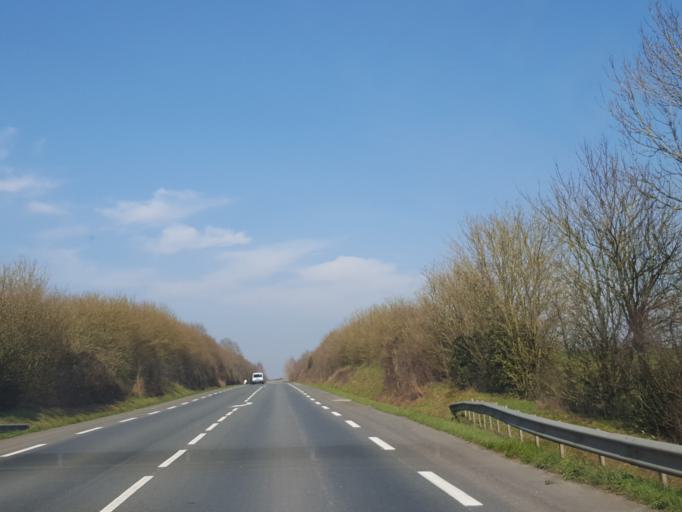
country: FR
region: Pays de la Loire
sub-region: Departement de la Vendee
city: Saint-Fulgent
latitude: 46.8395
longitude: -1.1620
